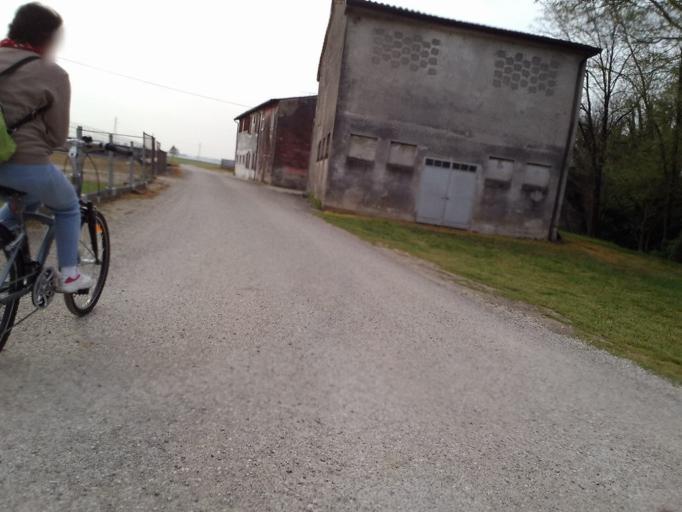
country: IT
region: Veneto
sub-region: Provincia di Verona
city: Villafranca di Verona
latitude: 45.3394
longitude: 10.8553
